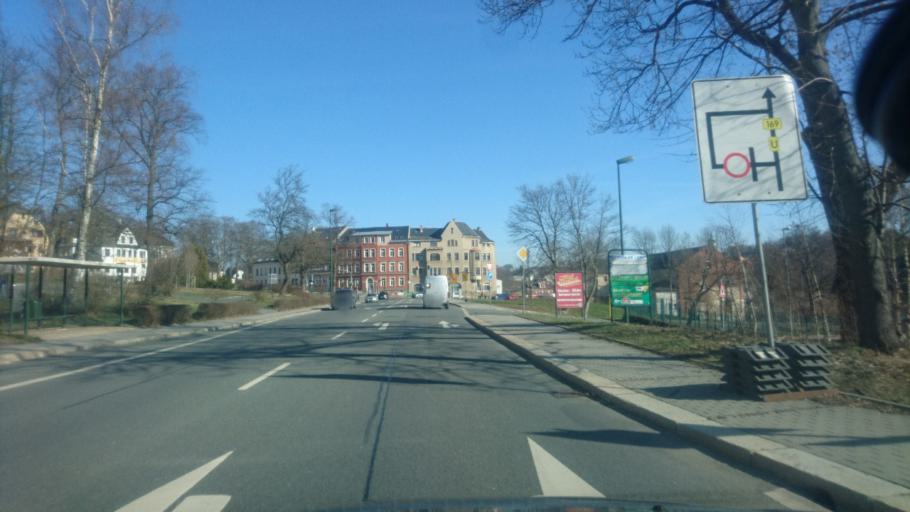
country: DE
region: Saxony
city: Auerbach
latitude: 50.5014
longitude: 12.3973
